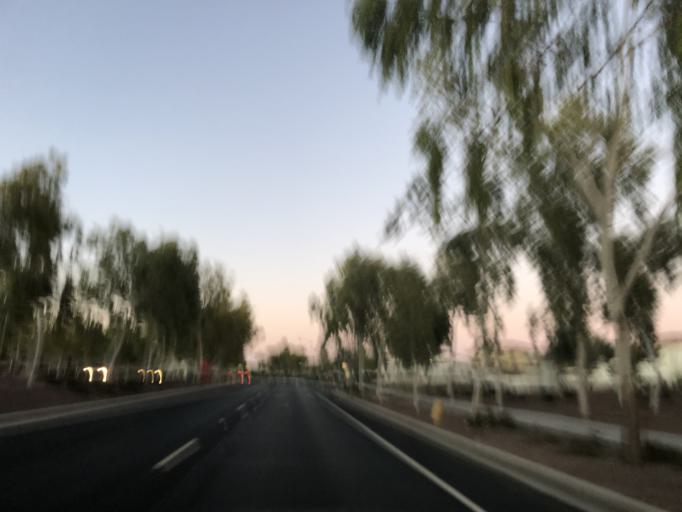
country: US
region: Arizona
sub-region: Maricopa County
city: Citrus Park
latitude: 33.4727
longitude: -112.5038
